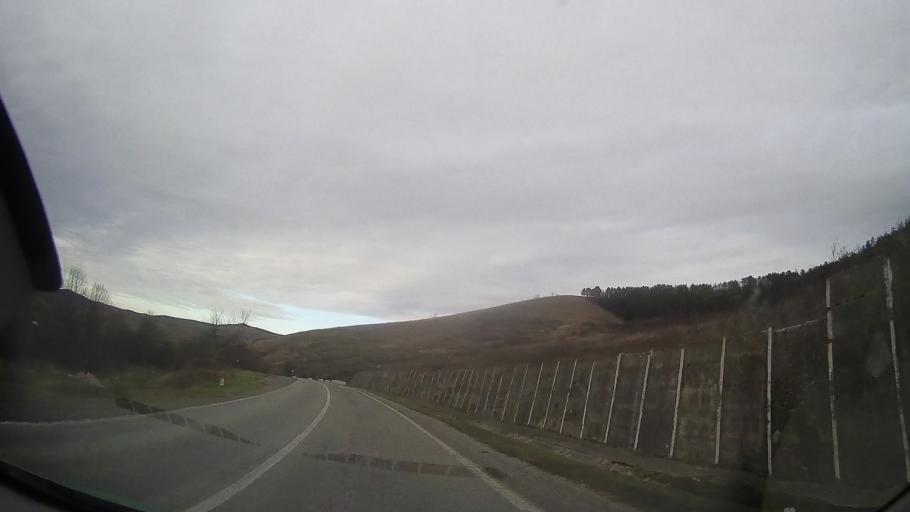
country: RO
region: Mures
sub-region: Comuna Sarmasu
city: Sarmasu
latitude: 46.7934
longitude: 24.1846
